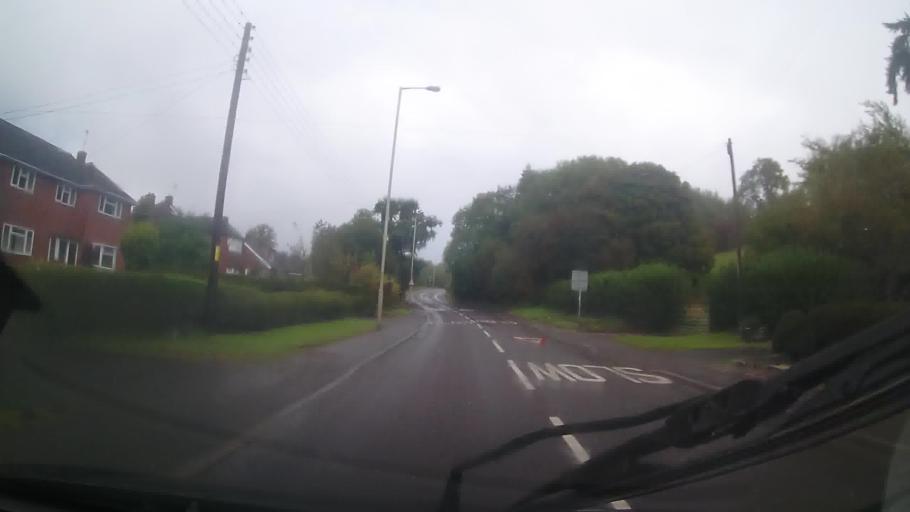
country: GB
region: England
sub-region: Shropshire
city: Much Wenlock
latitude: 52.6036
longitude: -2.5574
